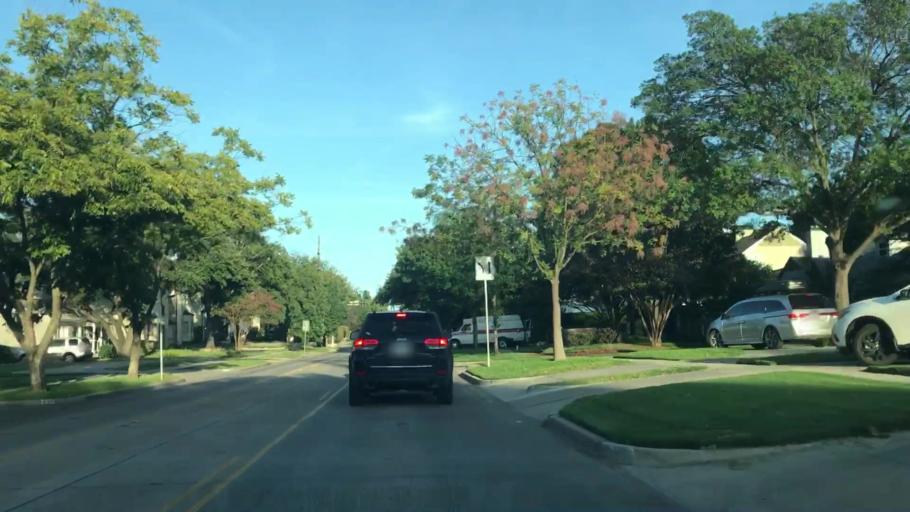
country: US
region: Texas
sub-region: Dallas County
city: University Park
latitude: 32.8511
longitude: -96.7784
